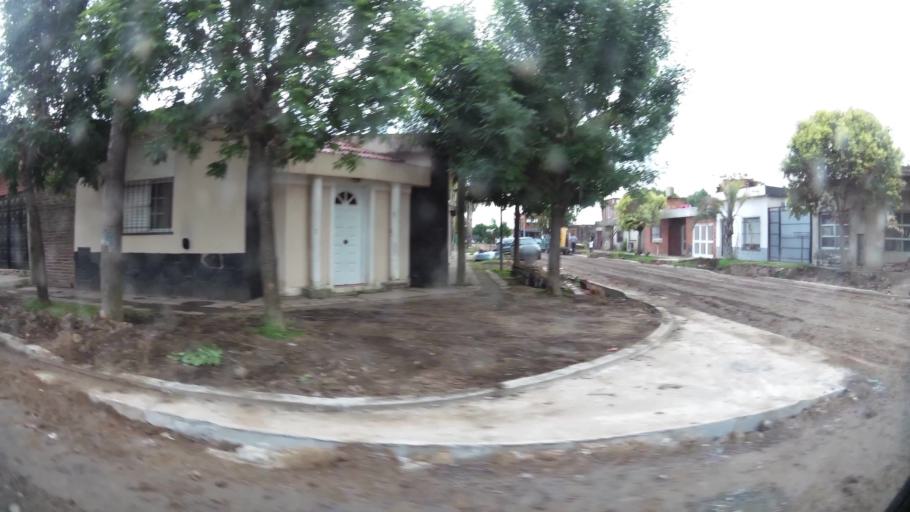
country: AR
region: Buenos Aires
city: San Nicolas de los Arroyos
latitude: -33.3674
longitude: -60.2002
